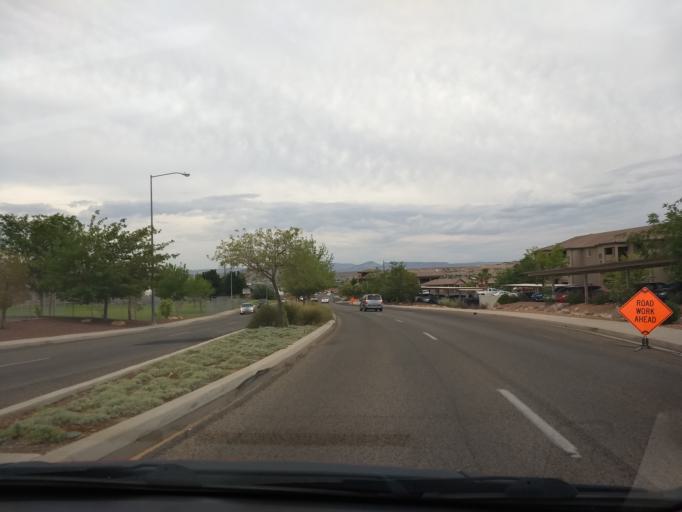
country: US
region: Utah
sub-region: Washington County
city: Washington
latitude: 37.1025
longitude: -113.5399
